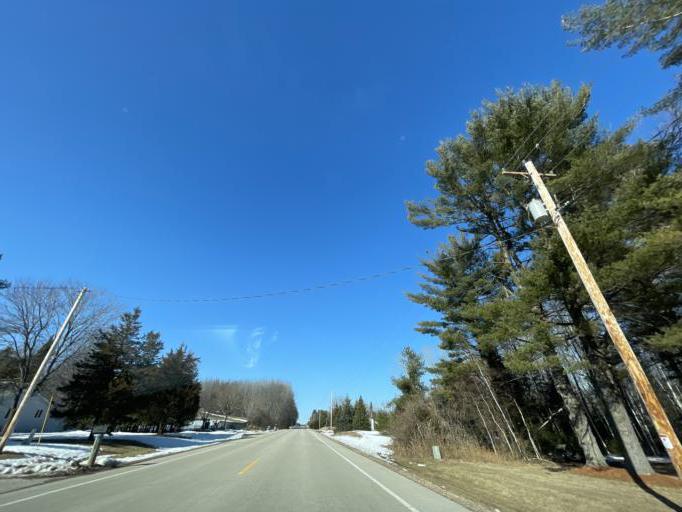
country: US
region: Wisconsin
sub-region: Brown County
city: Suamico
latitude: 44.6522
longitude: -88.0902
